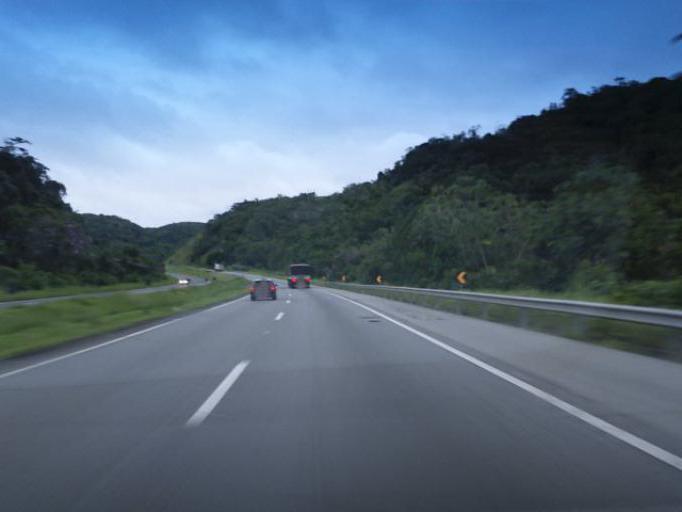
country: BR
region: Sao Paulo
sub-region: Miracatu
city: Miracatu
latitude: -24.2387
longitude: -47.3614
